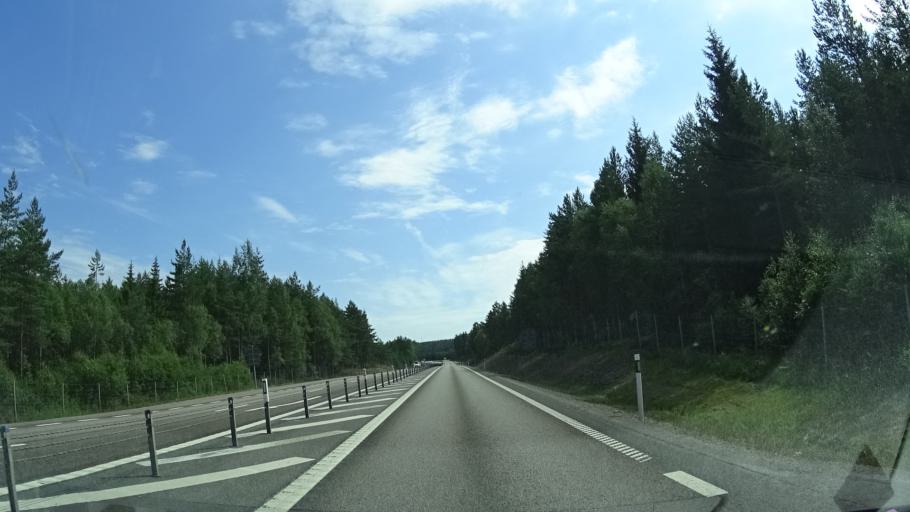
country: SE
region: Vaermland
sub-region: Kristinehamns Kommun
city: Kristinehamn
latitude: 59.3114
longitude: 14.1886
